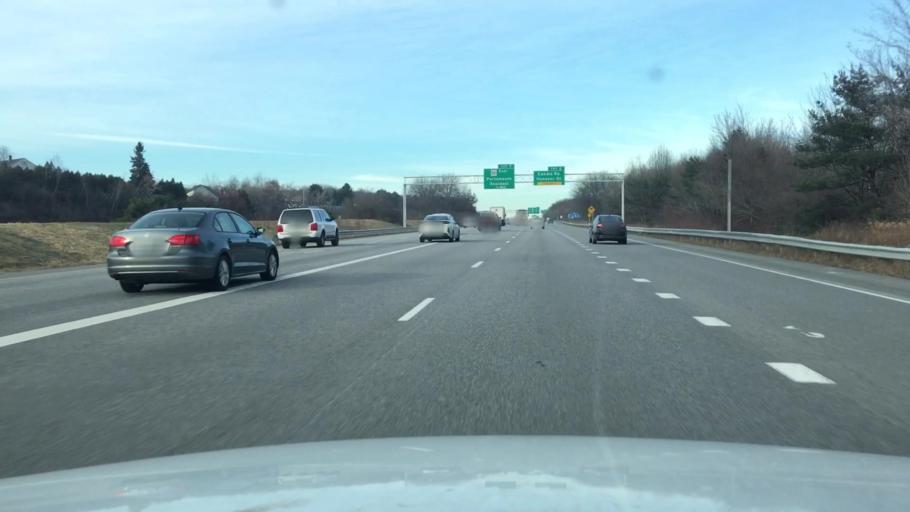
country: US
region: New Hampshire
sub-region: Hillsborough County
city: Manchester
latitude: 42.9697
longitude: -71.4127
